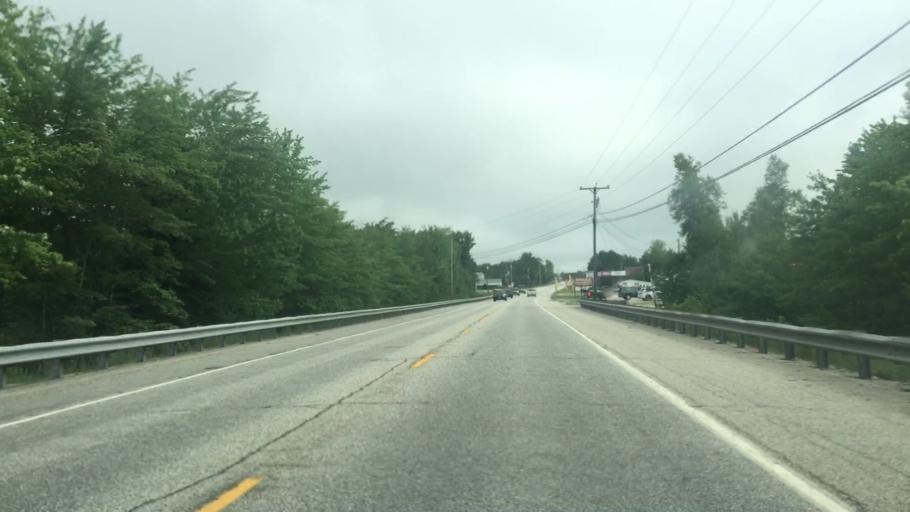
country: US
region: Maine
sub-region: Oxford County
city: South Paris
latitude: 44.2349
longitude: -70.5139
